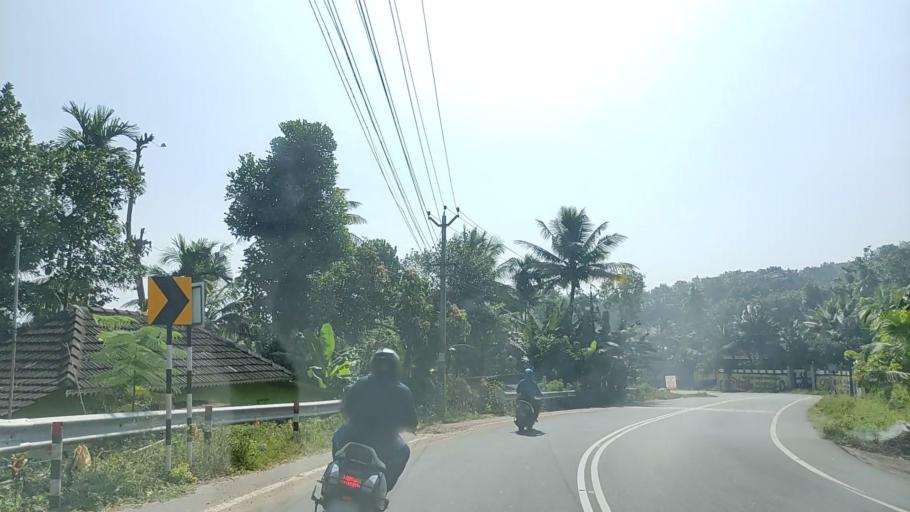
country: IN
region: Kerala
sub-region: Kollam
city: Punalur
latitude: 8.9359
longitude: 76.9530
